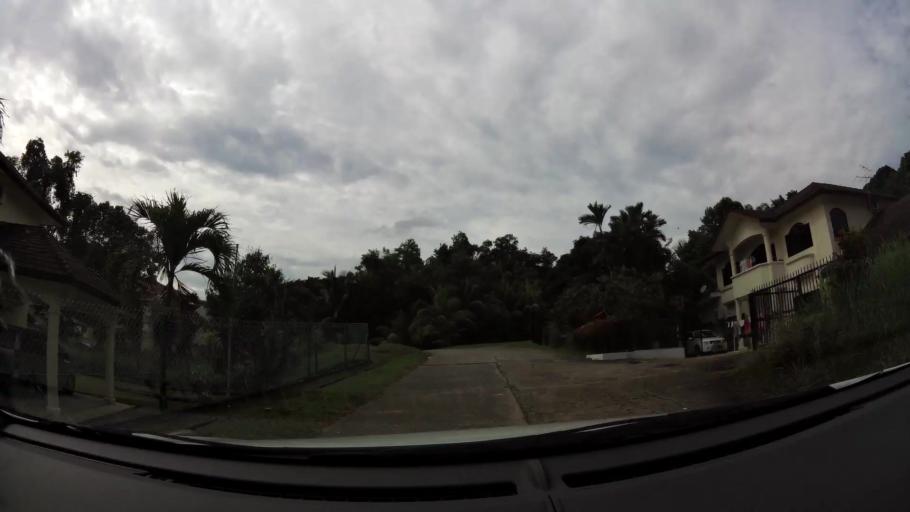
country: BN
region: Brunei and Muara
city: Bandar Seri Begawan
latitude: 4.8867
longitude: 114.8924
